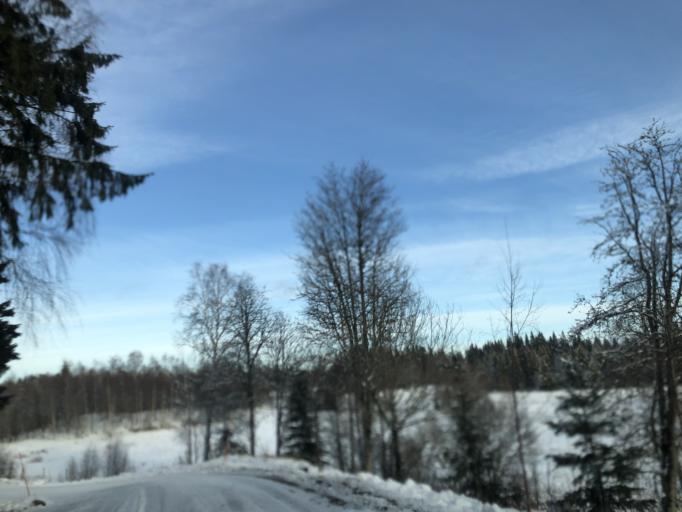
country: SE
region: Vaestra Goetaland
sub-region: Ulricehamns Kommun
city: Ulricehamn
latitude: 57.7682
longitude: 13.5211
